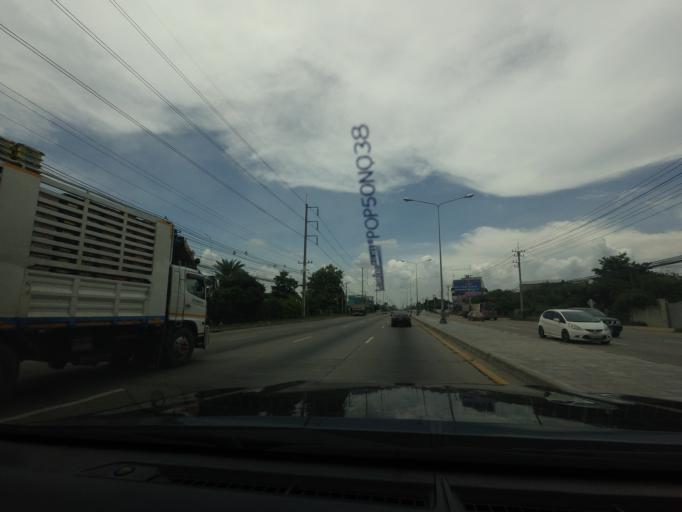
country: TH
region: Nakhon Pathom
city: Nakhon Pathom
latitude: 13.8460
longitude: 100.0233
